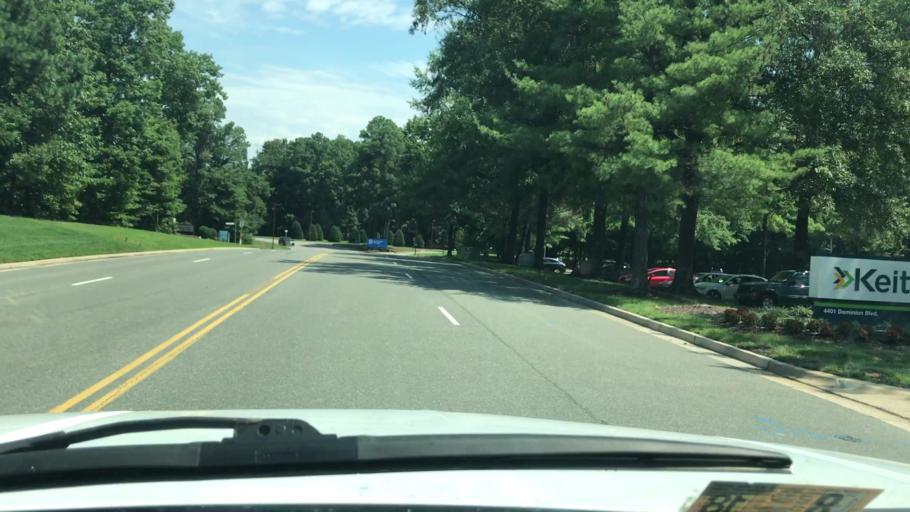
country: US
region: Virginia
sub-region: Henrico County
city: Short Pump
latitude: 37.6533
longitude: -77.5848
